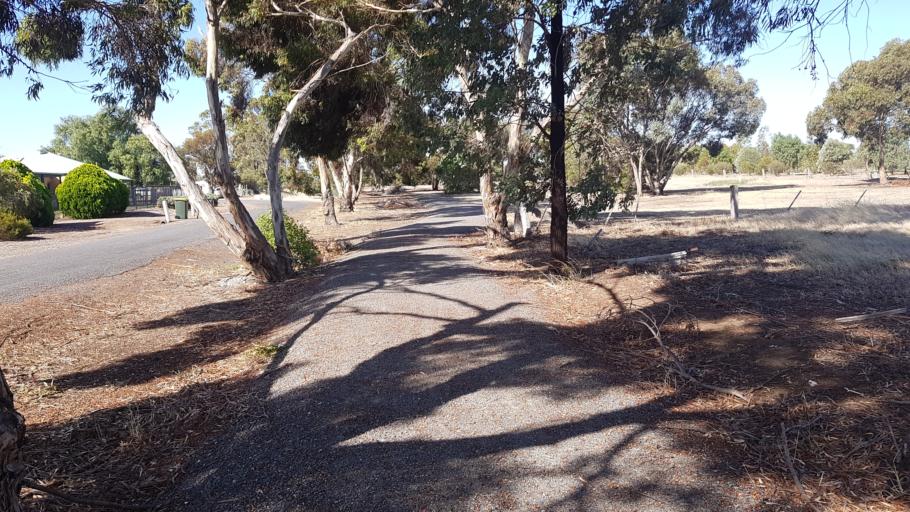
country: AU
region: Victoria
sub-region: Horsham
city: Horsham
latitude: -36.7462
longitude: 141.9375
